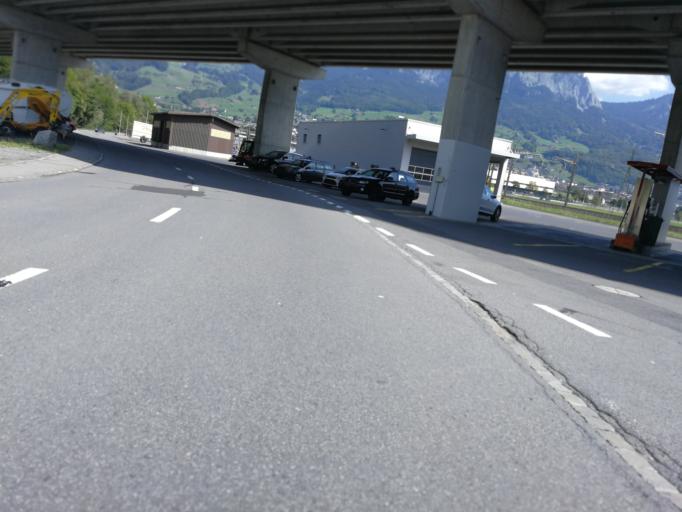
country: CH
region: Schwyz
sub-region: Bezirk Schwyz
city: Ingenbohl
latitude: 47.0160
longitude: 8.6258
